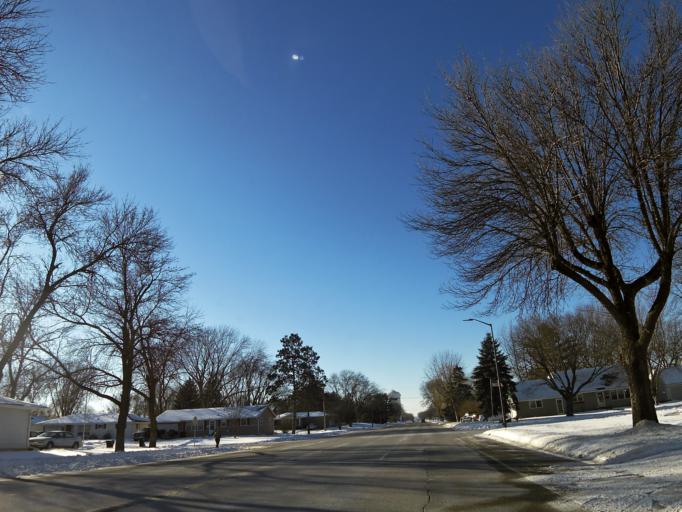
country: US
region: Minnesota
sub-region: Scott County
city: Shakopee
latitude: 44.7884
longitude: -93.5285
